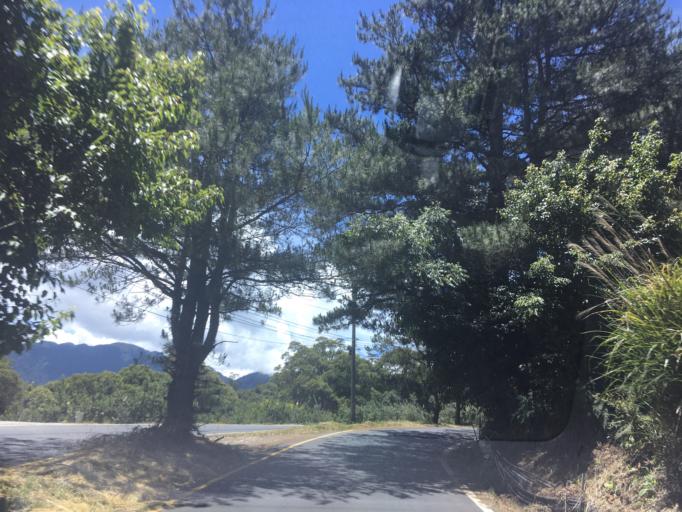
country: TW
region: Taiwan
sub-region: Nantou
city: Puli
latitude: 24.2351
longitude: 121.2439
